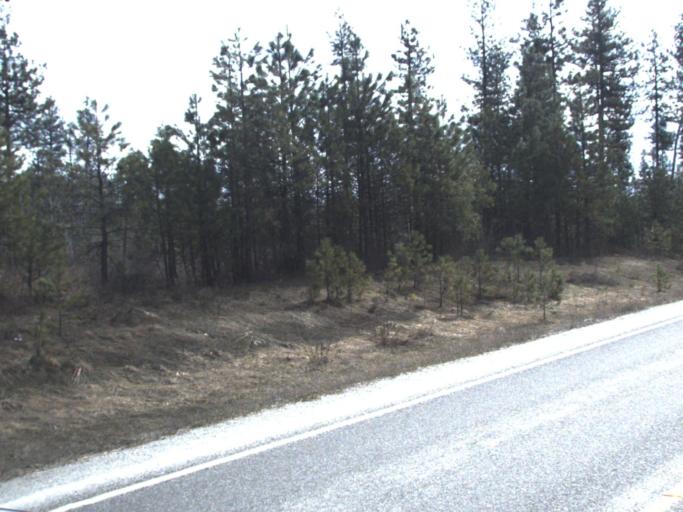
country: US
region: Washington
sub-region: Pend Oreille County
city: Newport
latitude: 48.3171
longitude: -117.2919
